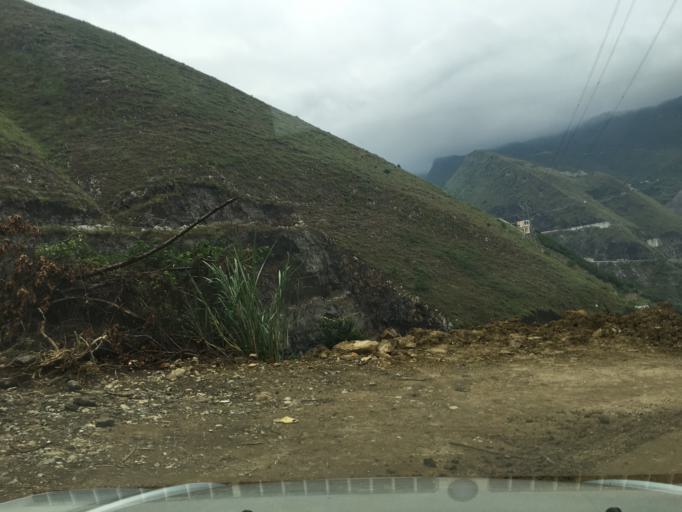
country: CN
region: Guizhou Sheng
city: Anshun
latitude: 25.9621
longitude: 105.2423
